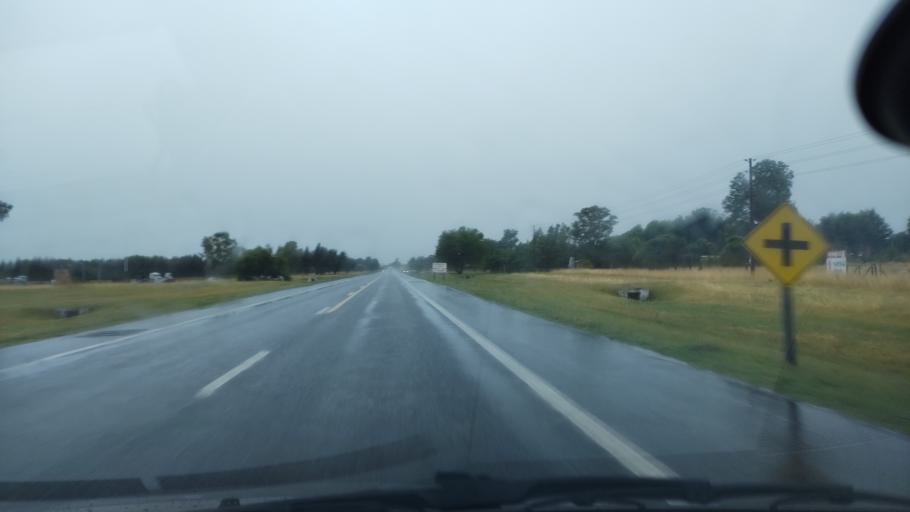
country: AR
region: Buenos Aires
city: Canuelas
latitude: -35.0583
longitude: -58.7975
